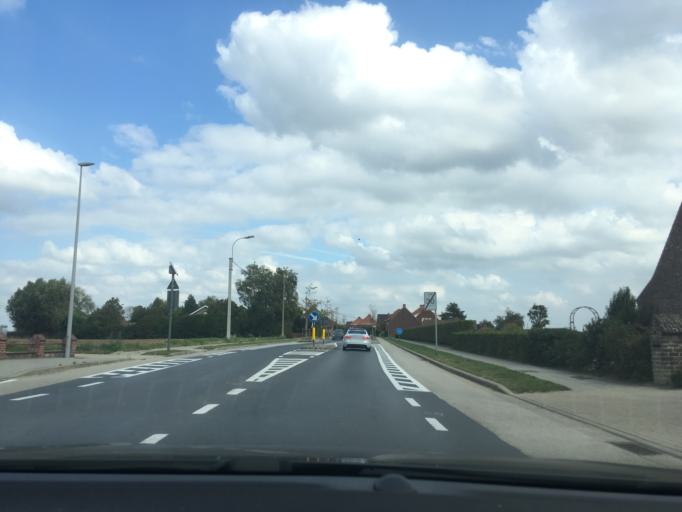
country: BE
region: Flanders
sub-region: Provincie West-Vlaanderen
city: Ieper
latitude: 50.8663
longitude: 2.9085
